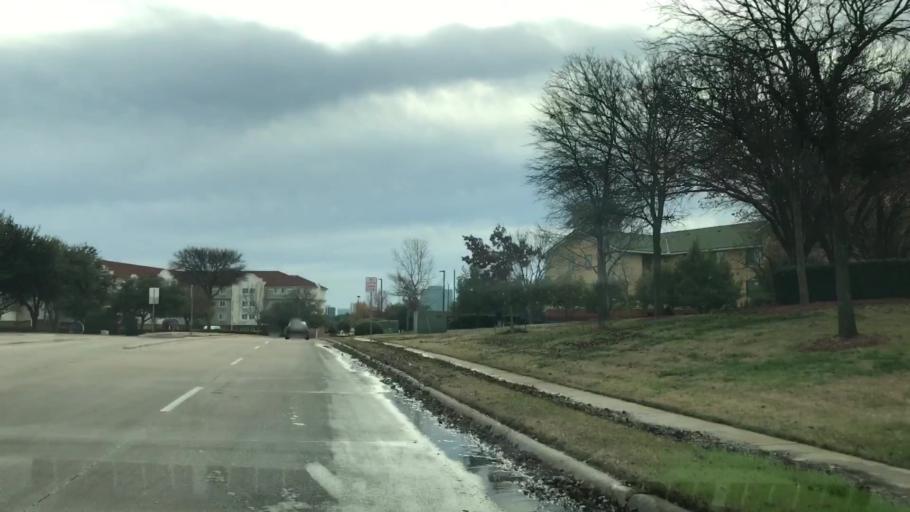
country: US
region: Texas
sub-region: Dallas County
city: Irving
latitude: 32.8842
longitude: -96.9548
